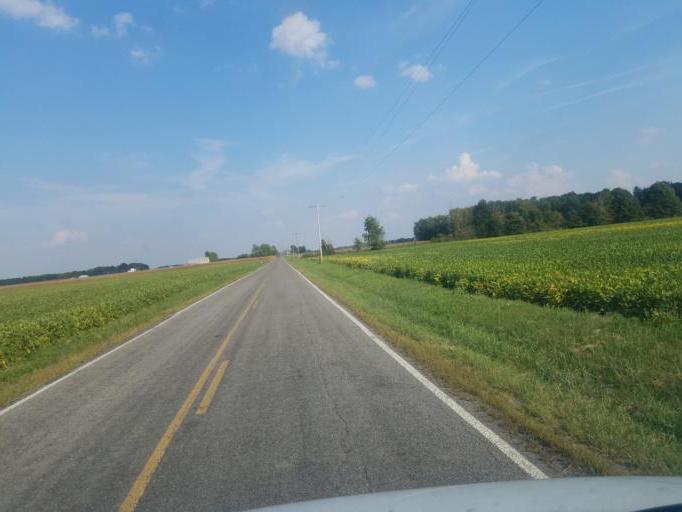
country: US
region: Ohio
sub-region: Hardin County
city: Forest
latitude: 40.9051
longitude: -83.5145
